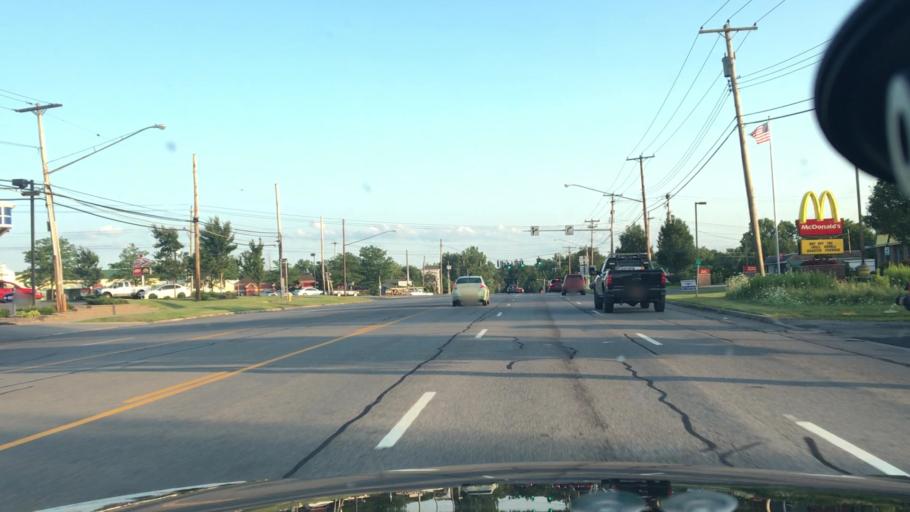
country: US
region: New York
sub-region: Erie County
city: Orchard Park
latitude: 42.7978
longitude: -78.7518
